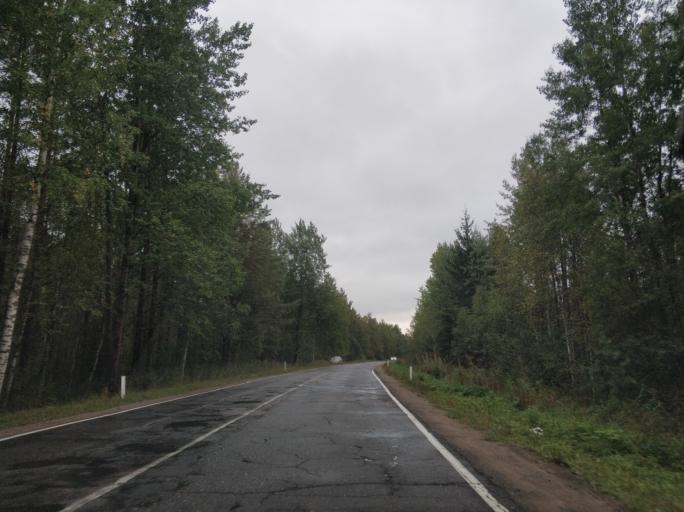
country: RU
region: Leningrad
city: Borisova Griva
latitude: 60.1628
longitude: 30.9217
